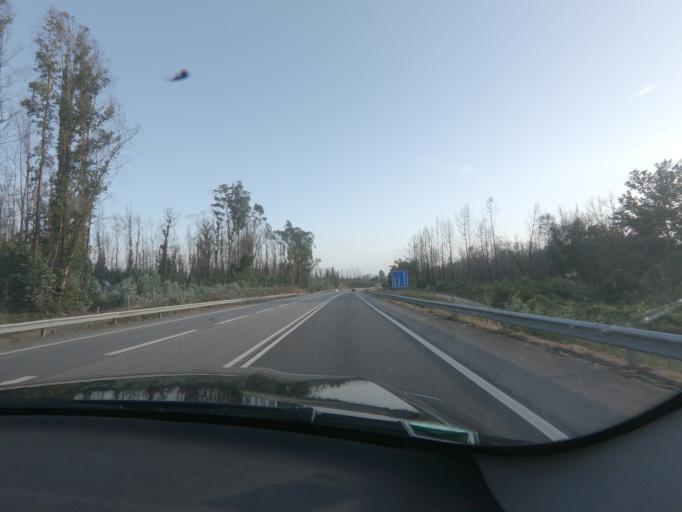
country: PT
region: Viseu
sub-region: Santa Comba Dao
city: Santa Comba Dao
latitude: 40.4284
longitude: -8.1155
